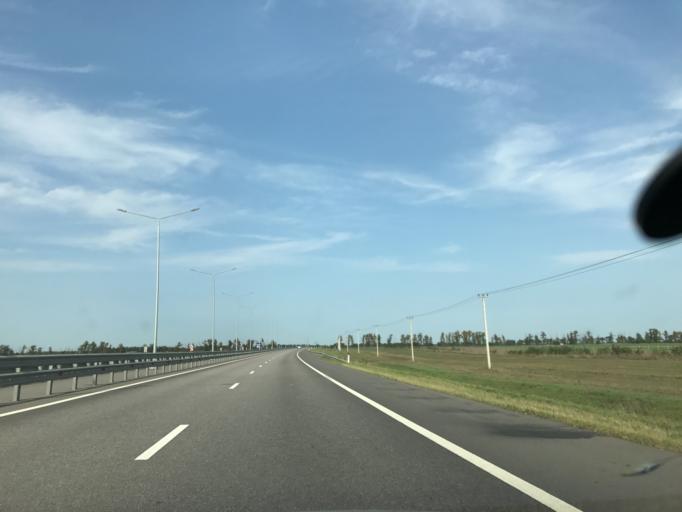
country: RU
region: Voronezj
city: Podkletnoye
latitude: 51.5173
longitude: 39.5113
